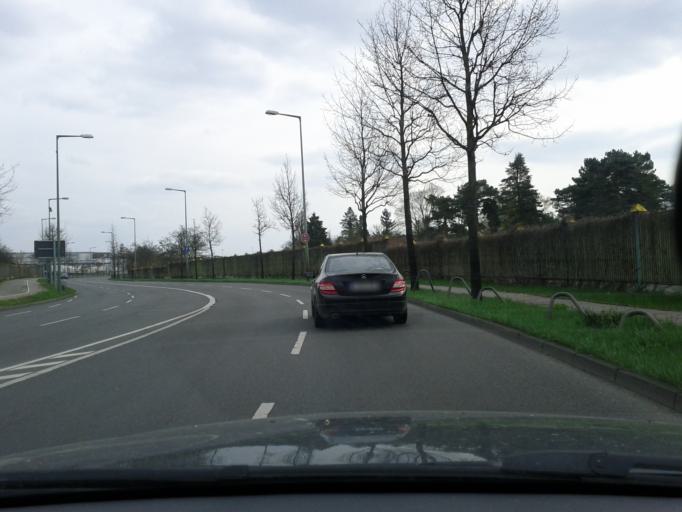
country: DE
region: Berlin
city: Westend
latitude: 52.5081
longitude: 13.2612
